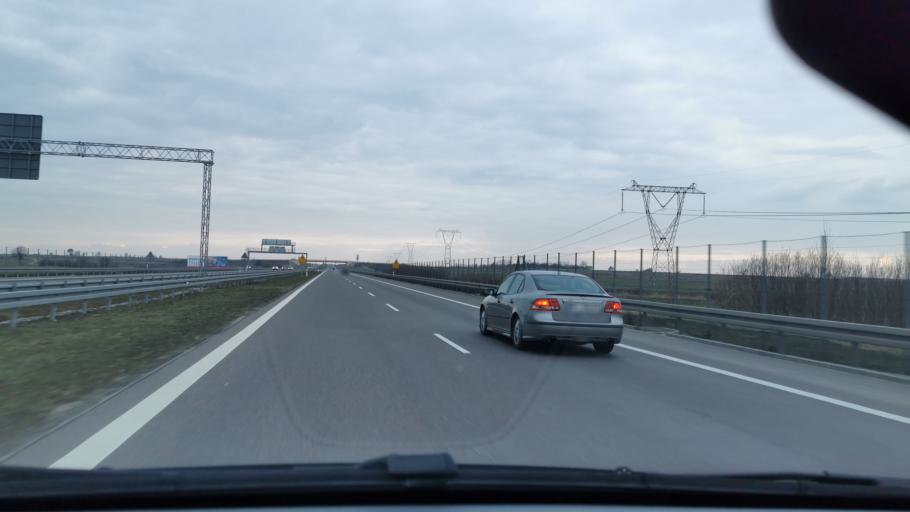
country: PL
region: Lublin Voivodeship
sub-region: Powiat pulawski
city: Markuszow
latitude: 51.3842
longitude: 22.2731
